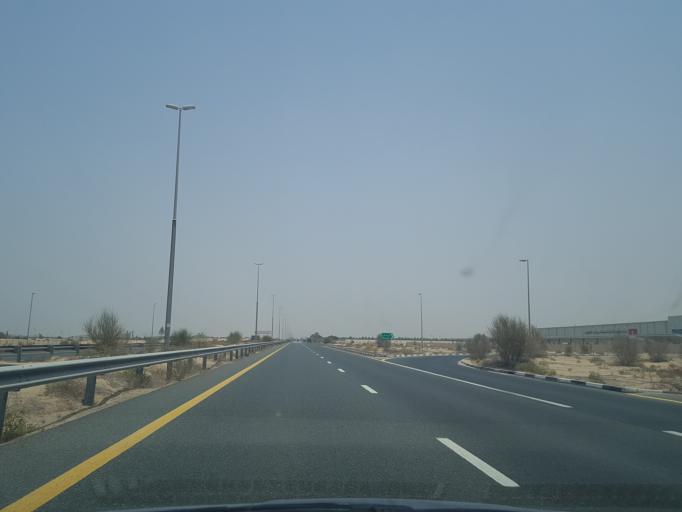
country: AE
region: Ash Shariqah
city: Sharjah
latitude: 25.1470
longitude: 55.4385
